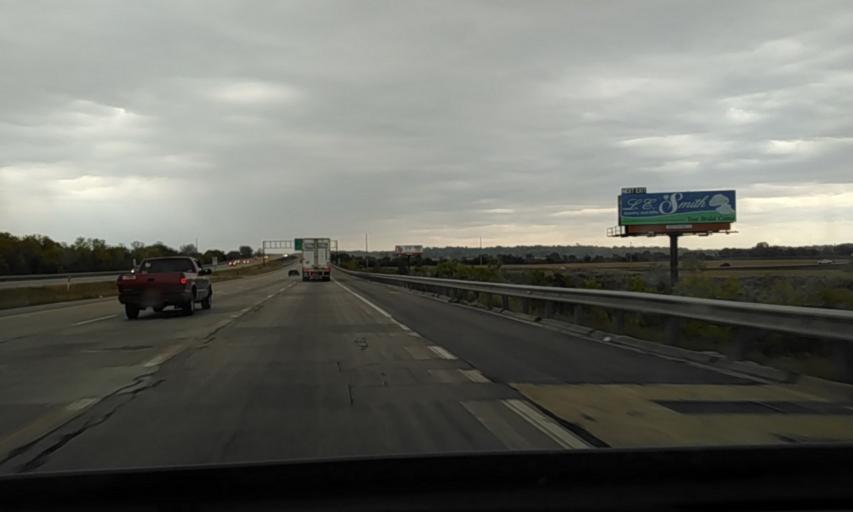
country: US
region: Illinois
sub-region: Saint Clair County
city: Caseyville
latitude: 38.6412
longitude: -90.0508
